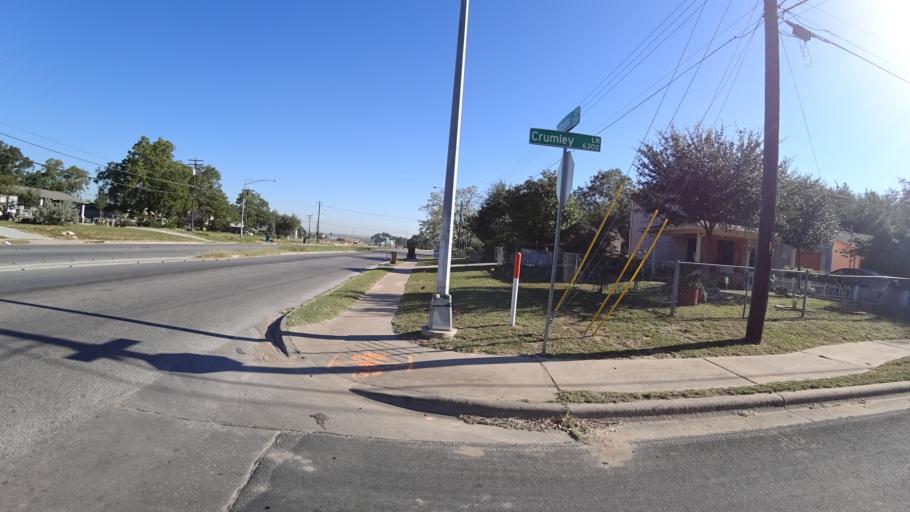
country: US
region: Texas
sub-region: Travis County
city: Austin
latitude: 30.2413
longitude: -97.6928
